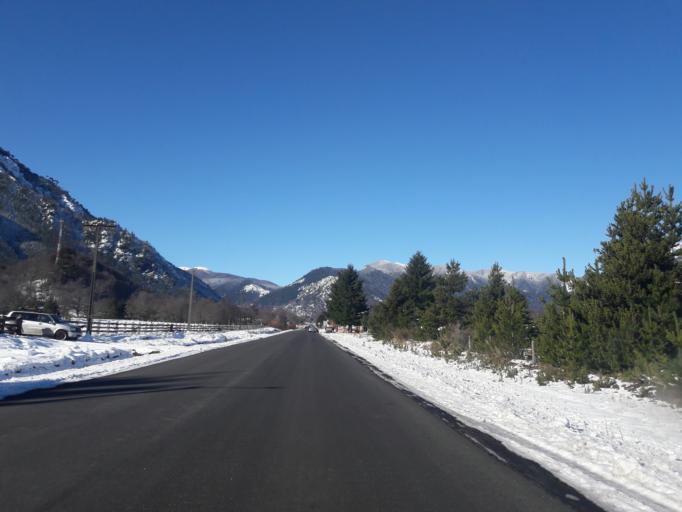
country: CL
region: Araucania
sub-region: Provincia de Cautin
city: Vilcun
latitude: -38.4717
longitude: -71.5709
